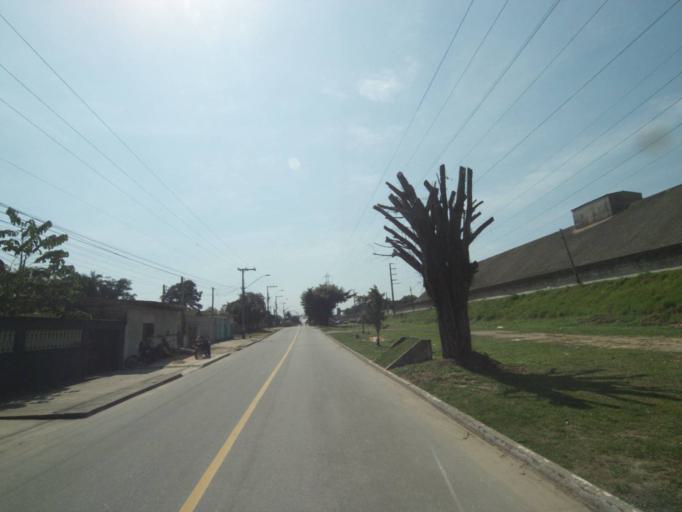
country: BR
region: Parana
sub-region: Paranagua
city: Paranagua
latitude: -25.5390
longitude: -48.5420
